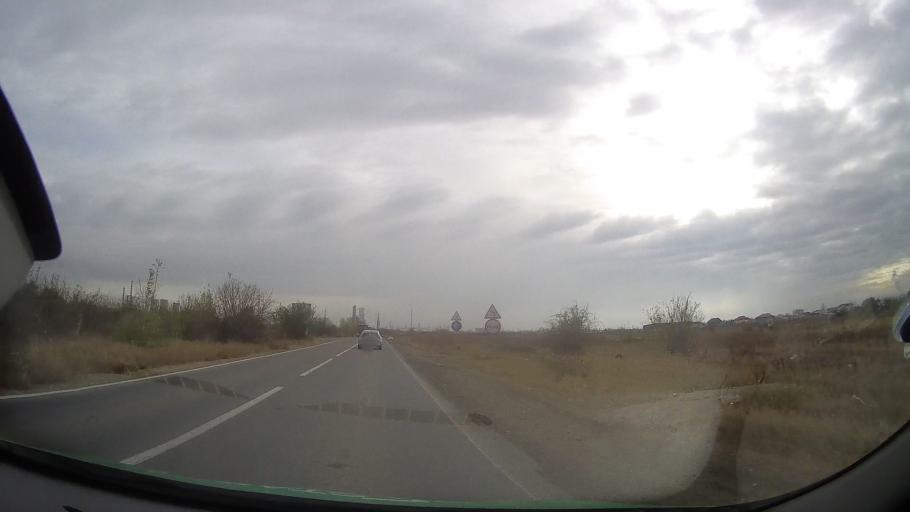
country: RO
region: Prahova
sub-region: Comuna Bucov
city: Bucov
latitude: 44.9547
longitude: 26.0522
